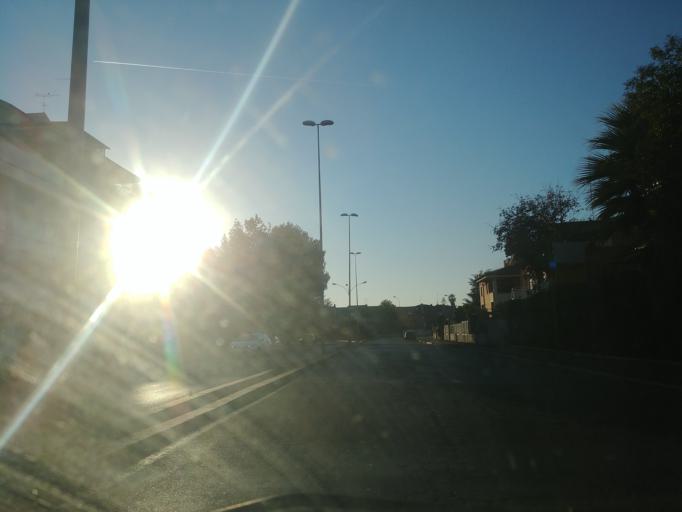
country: IT
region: Latium
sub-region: Provincia di Latina
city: Latina
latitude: 41.4576
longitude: 12.9052
